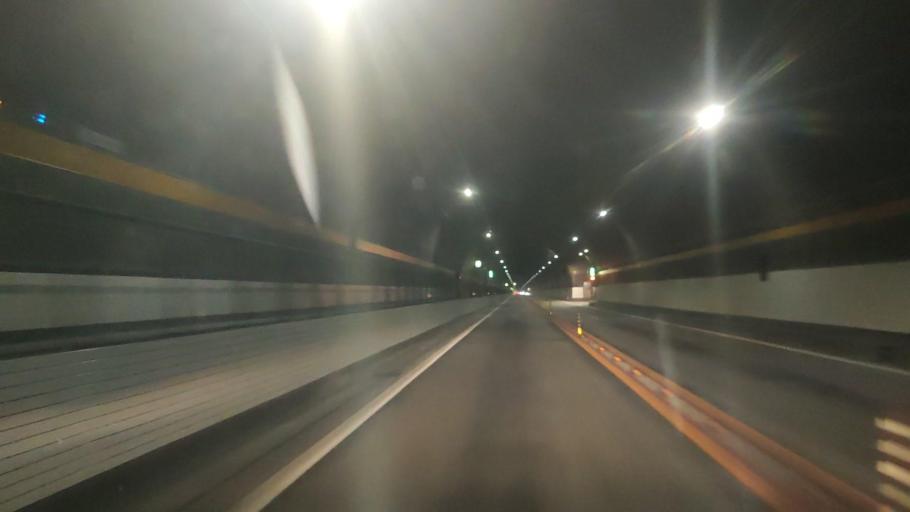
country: JP
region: Nagasaki
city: Obita
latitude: 32.7851
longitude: 129.8835
